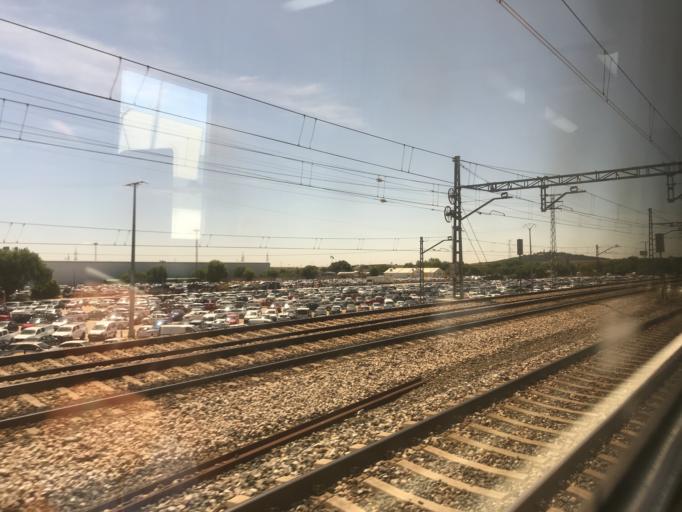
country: ES
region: Madrid
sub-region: Provincia de Madrid
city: Villaverde
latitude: 40.3382
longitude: -3.6839
